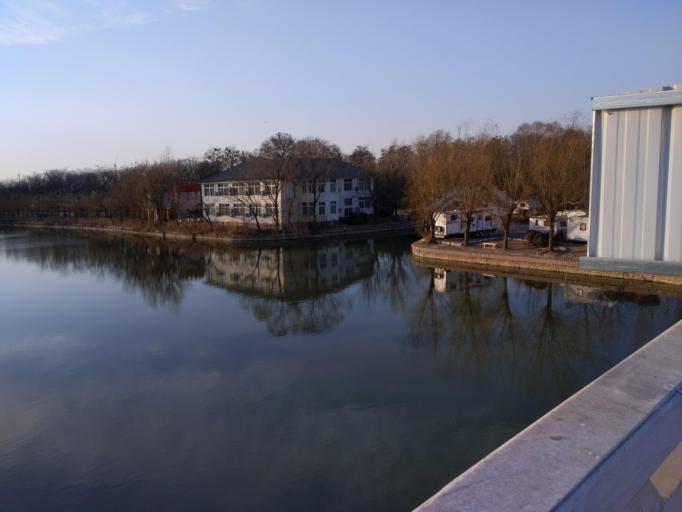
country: CN
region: Henan Sheng
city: Puyang
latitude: 35.7807
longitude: 114.9542
